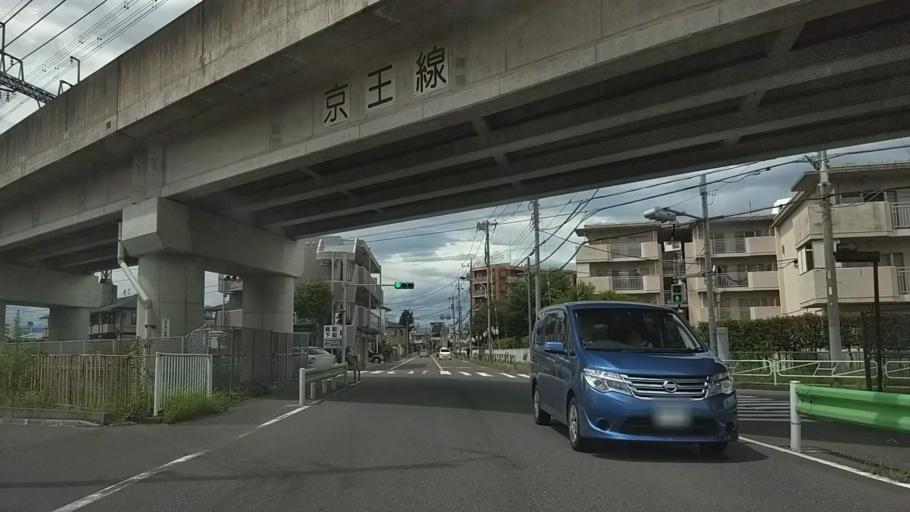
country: JP
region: Tokyo
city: Hachioji
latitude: 35.6426
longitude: 139.3629
